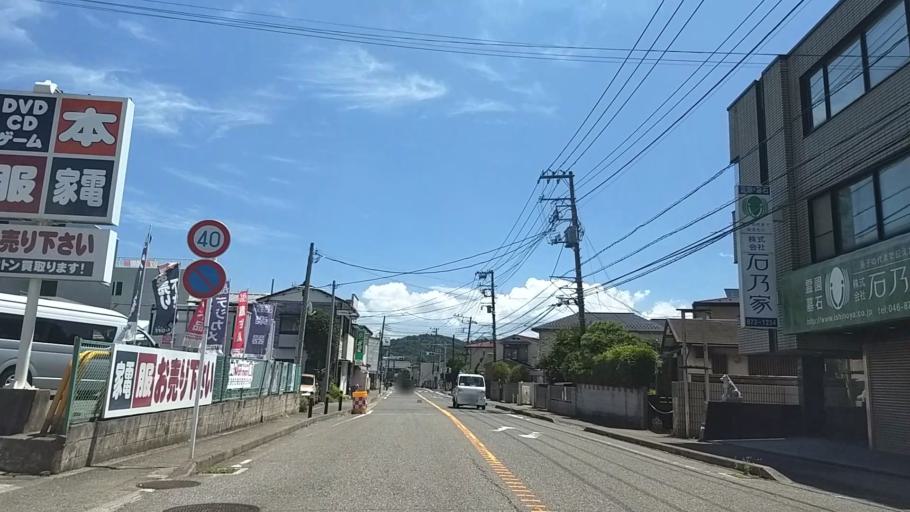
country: JP
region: Kanagawa
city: Zushi
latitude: 35.3011
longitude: 139.5705
